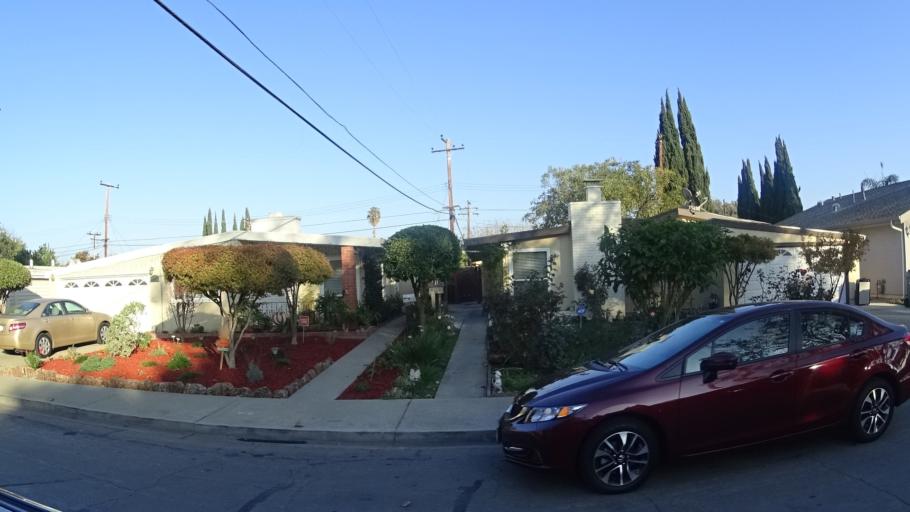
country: US
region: California
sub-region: Santa Clara County
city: Santa Clara
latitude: 37.3509
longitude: -121.9877
